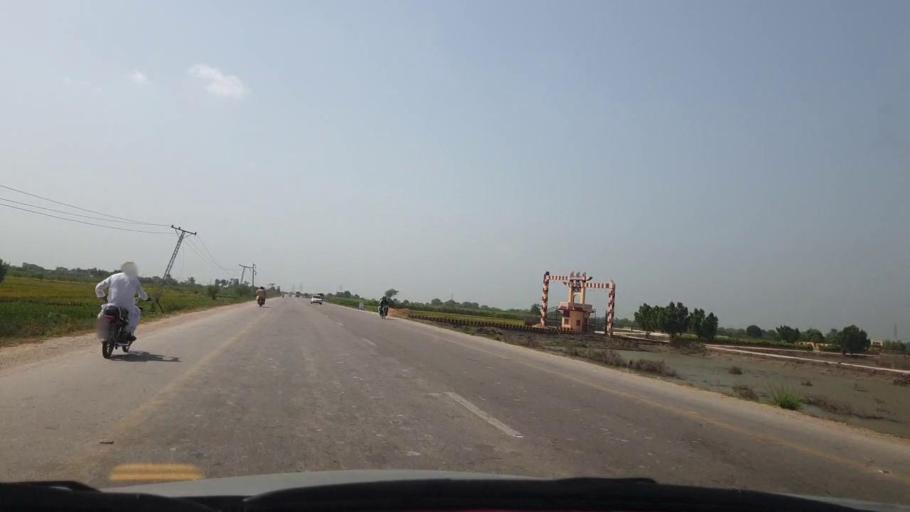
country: PK
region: Sindh
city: Matli
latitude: 25.0573
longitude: 68.6369
